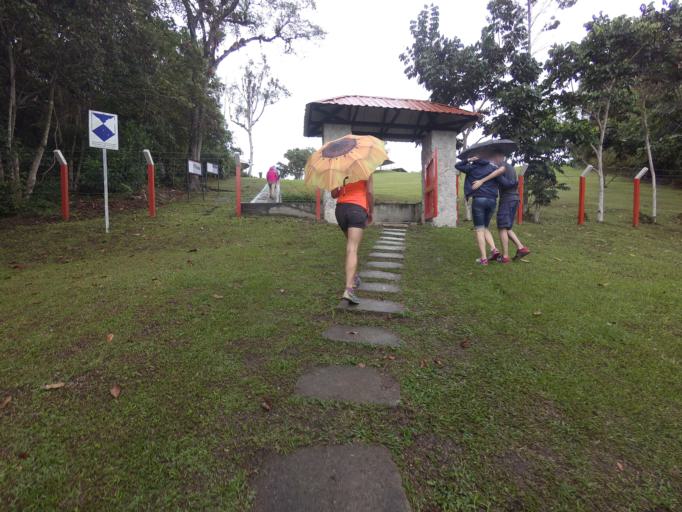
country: CO
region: Huila
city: Isnos
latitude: 1.9710
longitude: -76.2008
